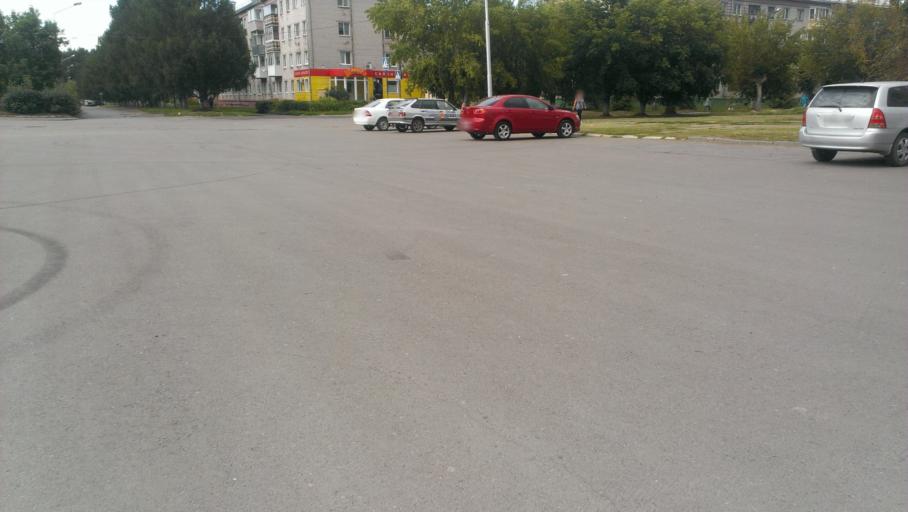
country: RU
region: Altai Krai
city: Yuzhnyy
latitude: 53.2546
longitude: 83.6939
